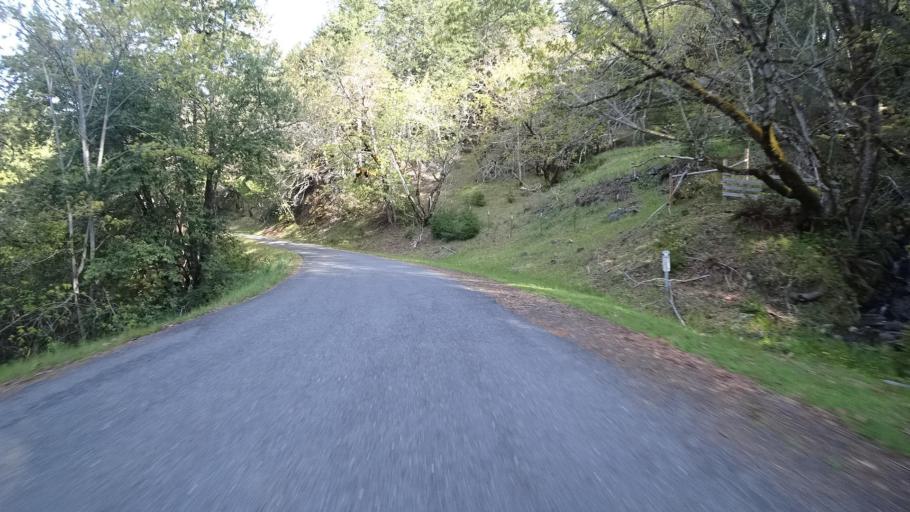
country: US
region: California
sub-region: Humboldt County
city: Hydesville
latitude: 40.6435
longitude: -123.9060
